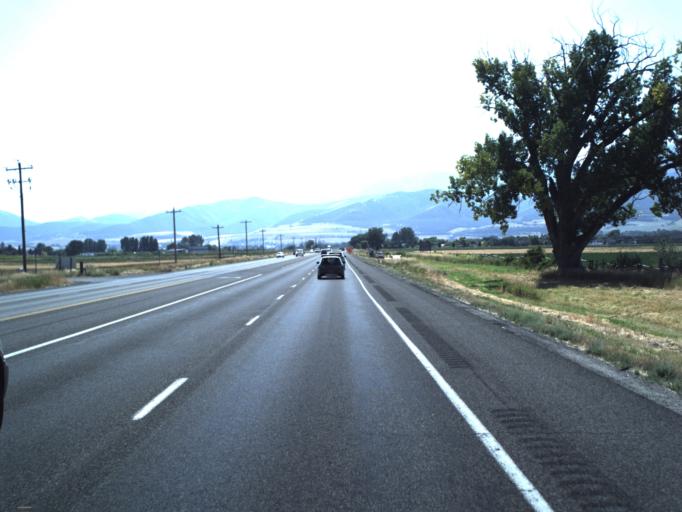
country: US
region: Utah
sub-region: Cache County
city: Wellsville
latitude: 41.6552
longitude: -111.9036
